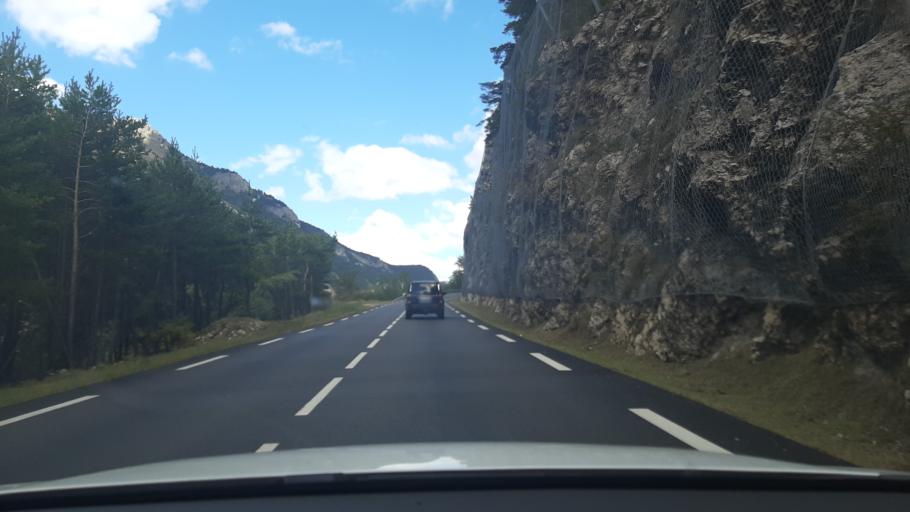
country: FR
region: Rhone-Alpes
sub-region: Departement de la Savoie
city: Modane
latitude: 45.2047
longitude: 6.6856
